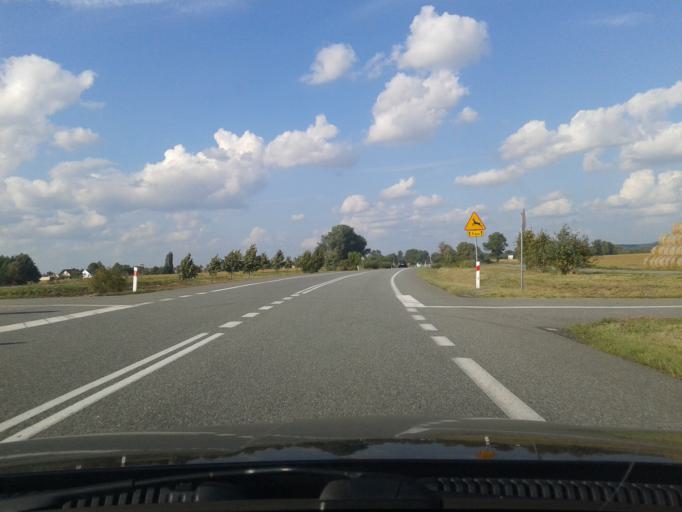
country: PL
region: Silesian Voivodeship
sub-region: Powiat raciborski
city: Chalupki
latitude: 49.9296
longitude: 18.3241
